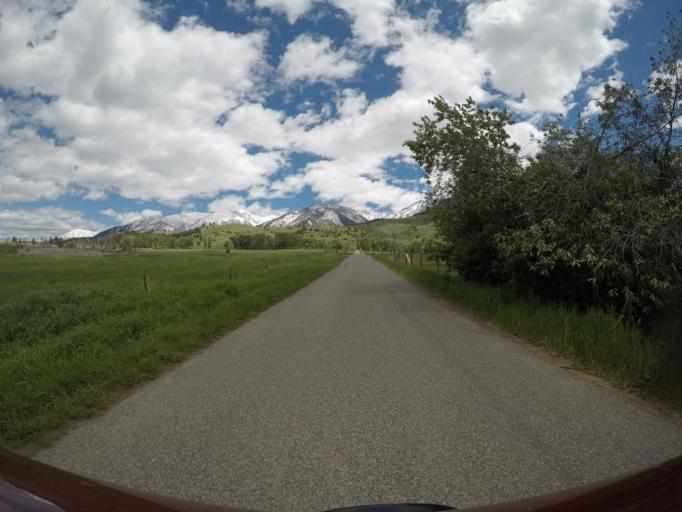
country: US
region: Montana
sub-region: Park County
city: Livingston
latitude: 45.4967
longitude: -110.5665
